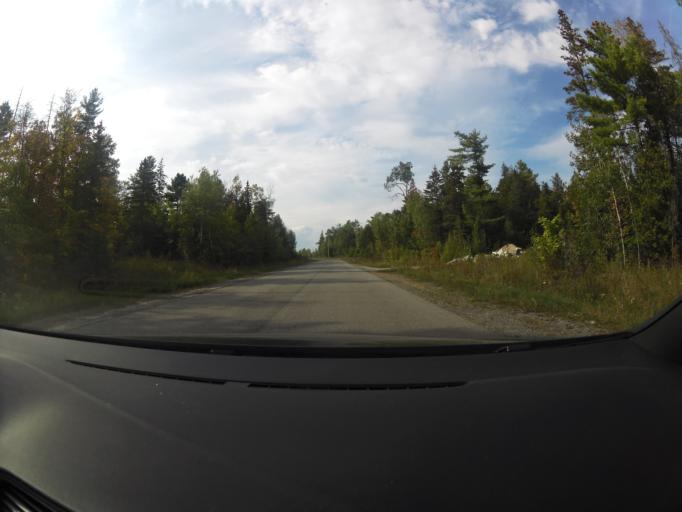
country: CA
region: Ontario
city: Carleton Place
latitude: 45.3389
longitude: -76.1583
